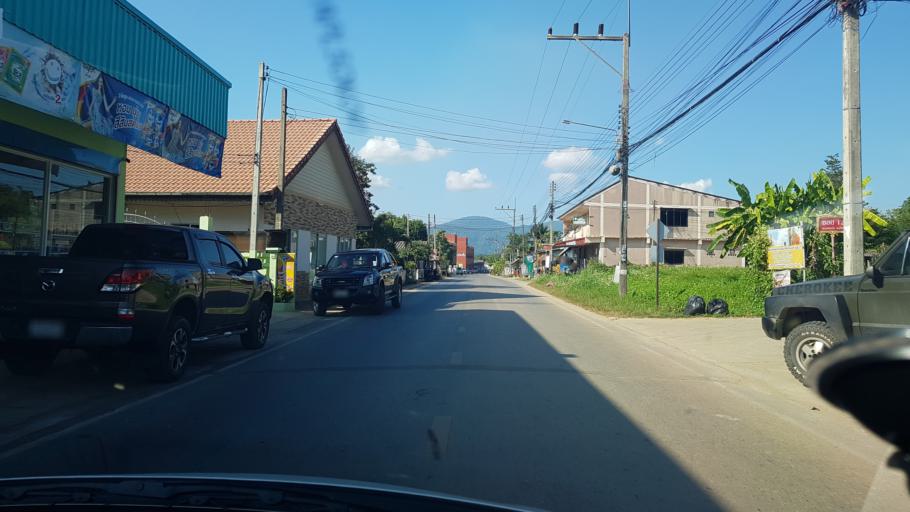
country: TH
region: Chiang Rai
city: Chiang Rai
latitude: 19.9480
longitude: 99.8101
